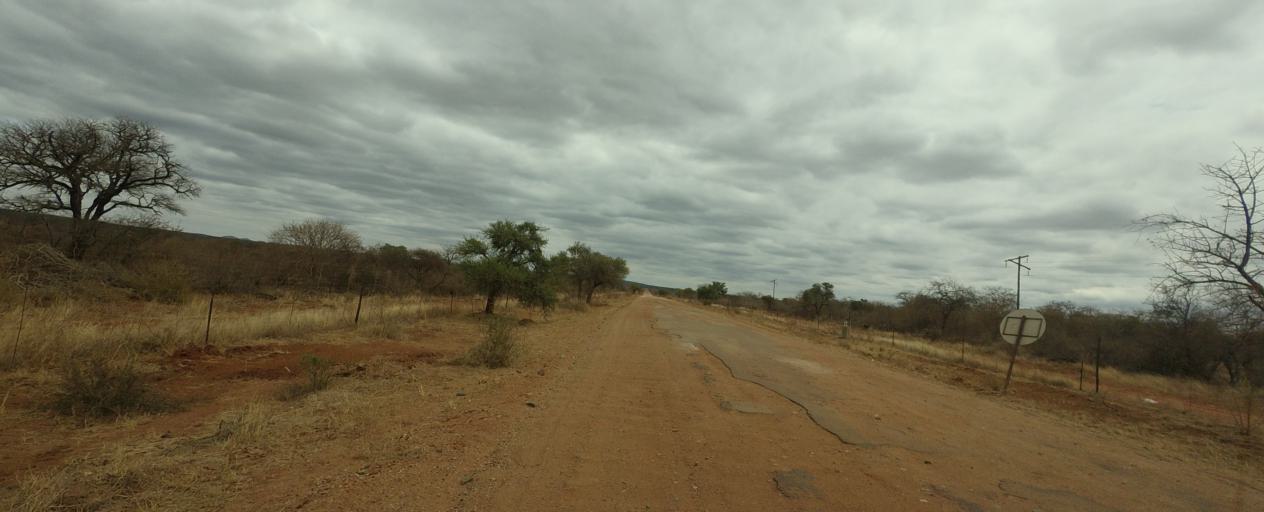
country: BW
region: Central
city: Mathathane
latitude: -22.7399
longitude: 28.4831
